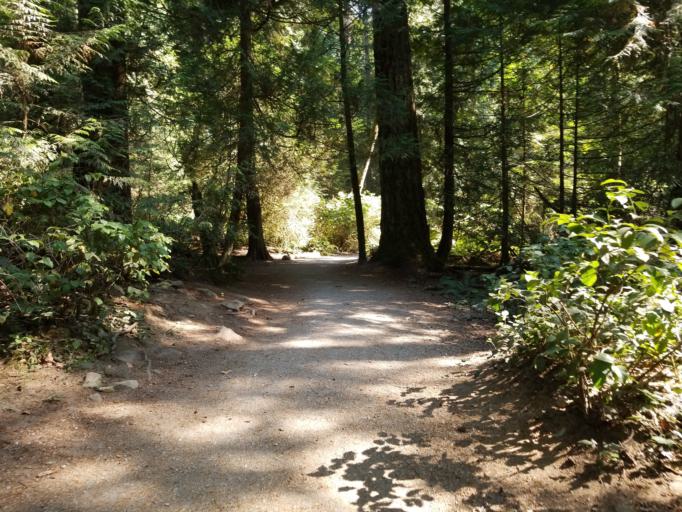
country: CA
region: British Columbia
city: West End
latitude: 49.2518
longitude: -123.2122
